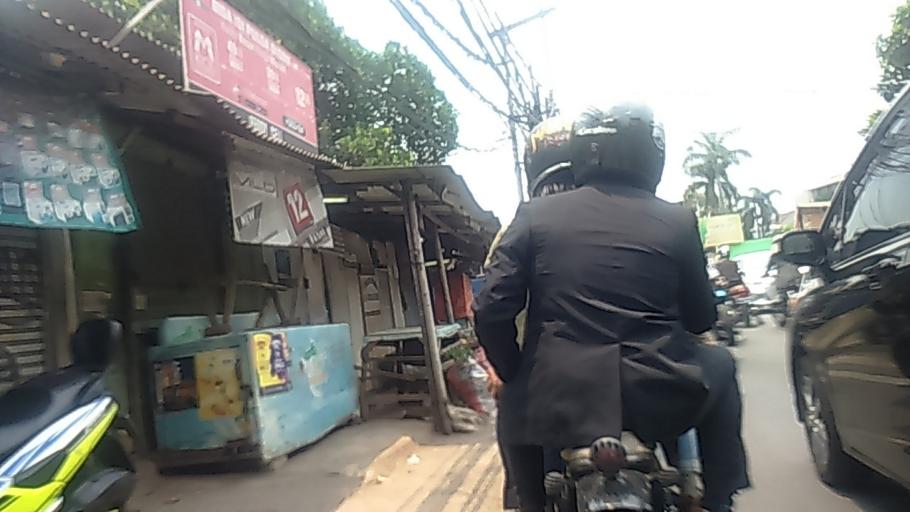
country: ID
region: West Java
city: Pamulang
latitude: -6.3010
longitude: 106.7743
